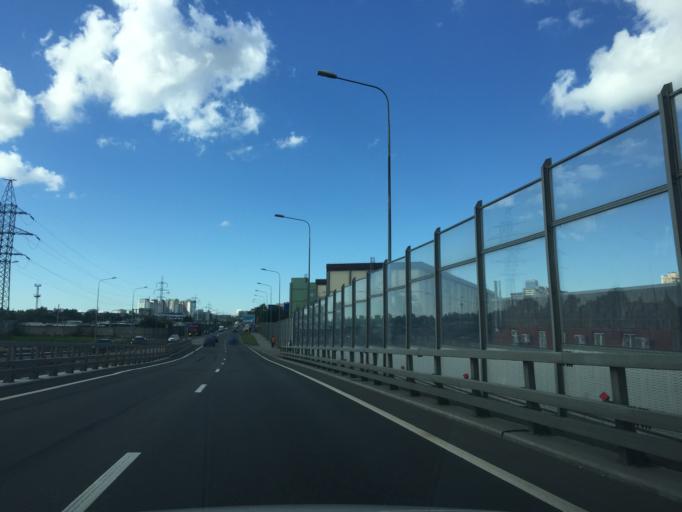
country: RU
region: St.-Petersburg
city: Dachnoye
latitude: 59.8343
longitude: 30.3076
